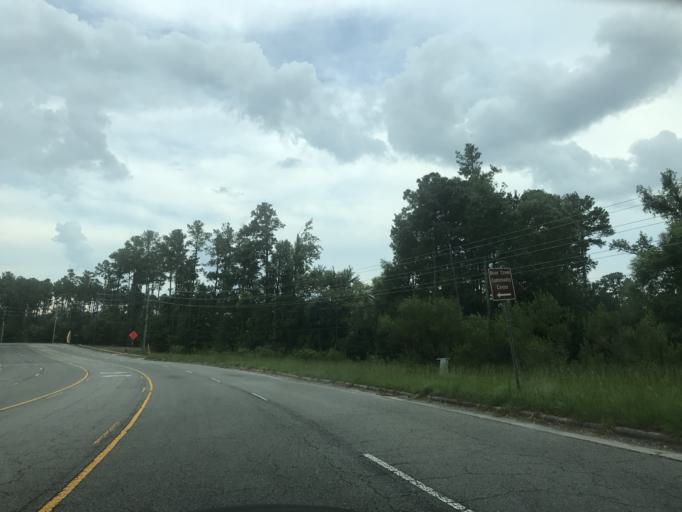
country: US
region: North Carolina
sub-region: Wake County
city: Morrisville
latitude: 35.8999
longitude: -78.8082
